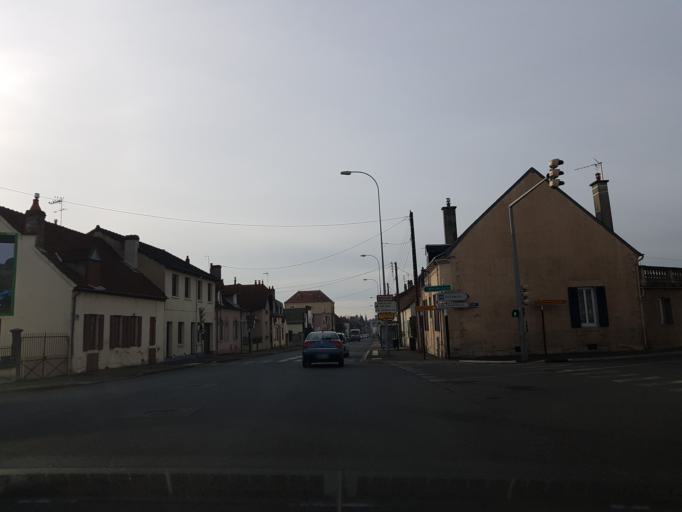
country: FR
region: Auvergne
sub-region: Departement de l'Allier
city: Yzeure
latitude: 46.5695
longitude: 3.3459
